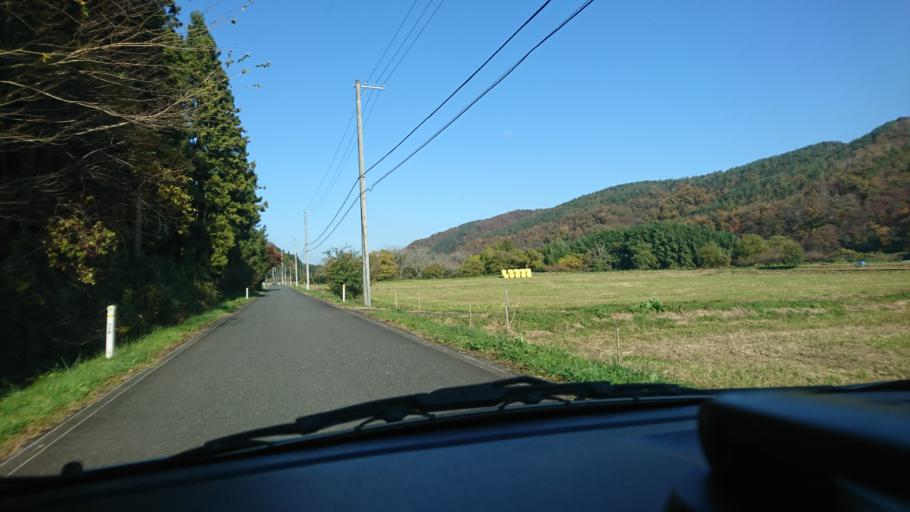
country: JP
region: Iwate
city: Ichinoseki
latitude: 38.8082
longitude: 141.2467
